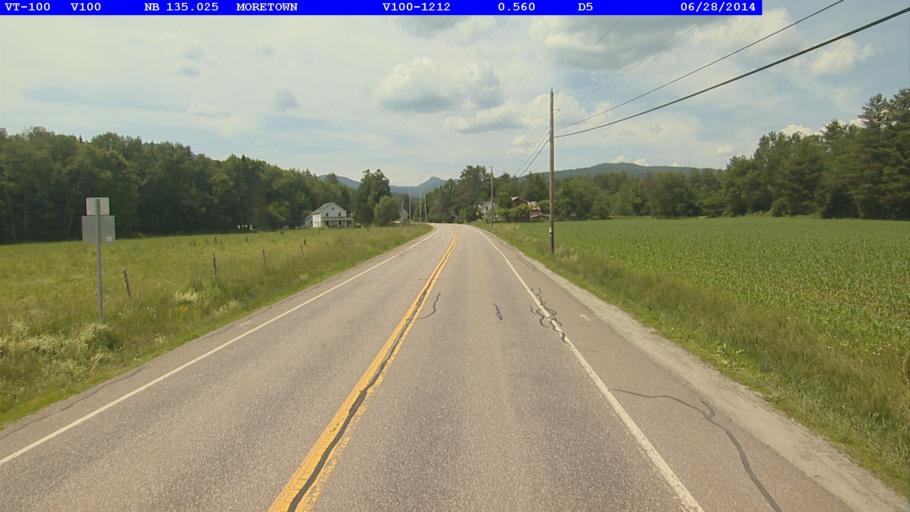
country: US
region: Vermont
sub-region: Washington County
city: Waterbury
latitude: 44.2411
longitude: -72.7771
